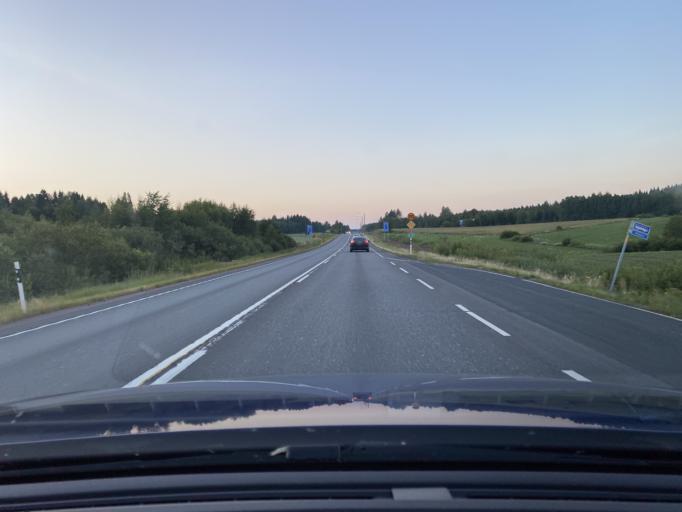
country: FI
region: Pirkanmaa
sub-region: Luoteis-Pirkanmaa
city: Ikaalinen
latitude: 61.8735
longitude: 22.9665
